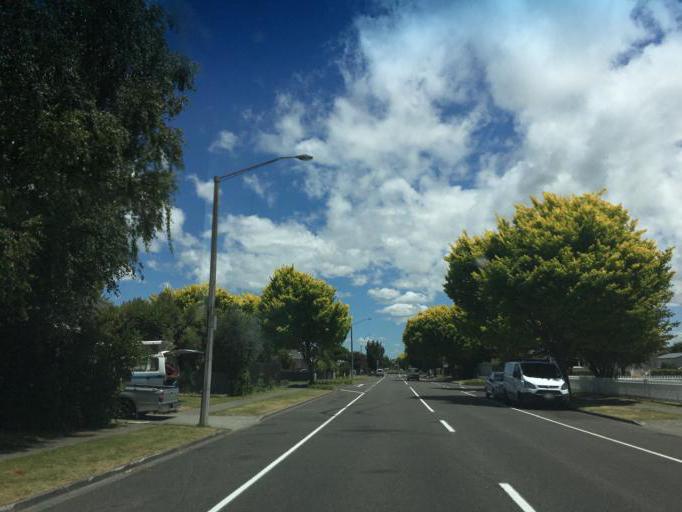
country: NZ
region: Hawke's Bay
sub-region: Hastings District
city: Hastings
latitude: -39.6465
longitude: 176.8562
